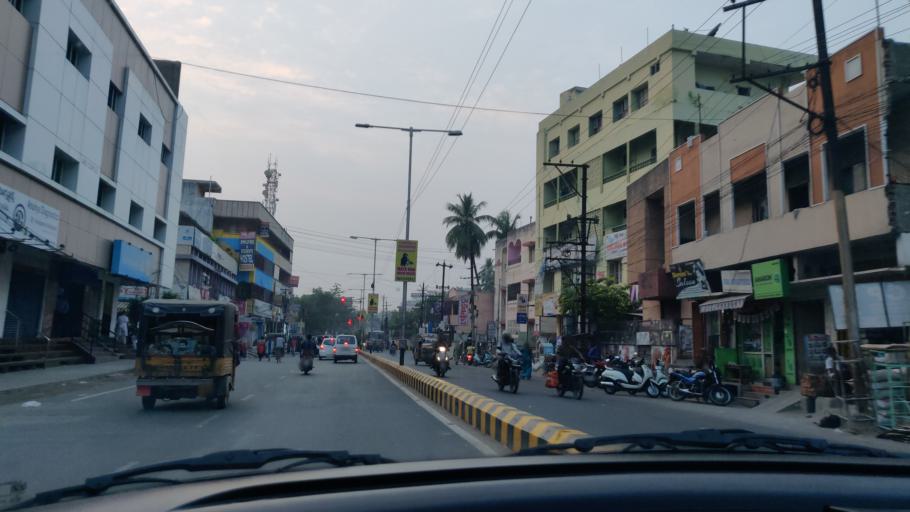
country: IN
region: Andhra Pradesh
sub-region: Krishna
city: Vijayawada
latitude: 16.5066
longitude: 80.6457
